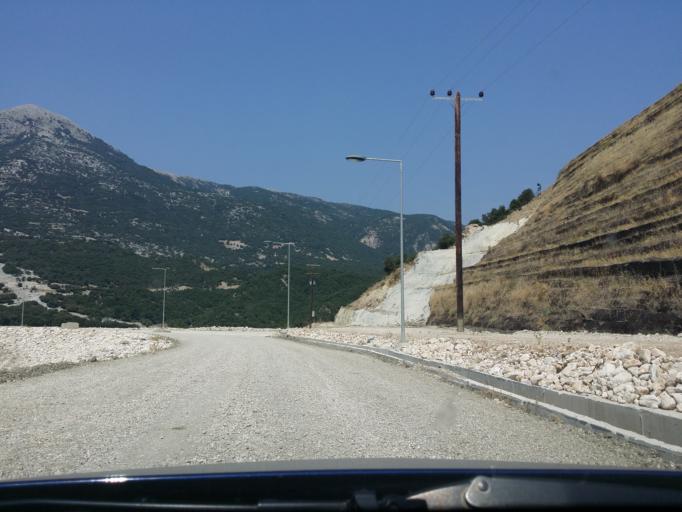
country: GR
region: West Greece
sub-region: Nomos Aitolias kai Akarnanias
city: Katouna
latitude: 38.7832
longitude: 21.0428
